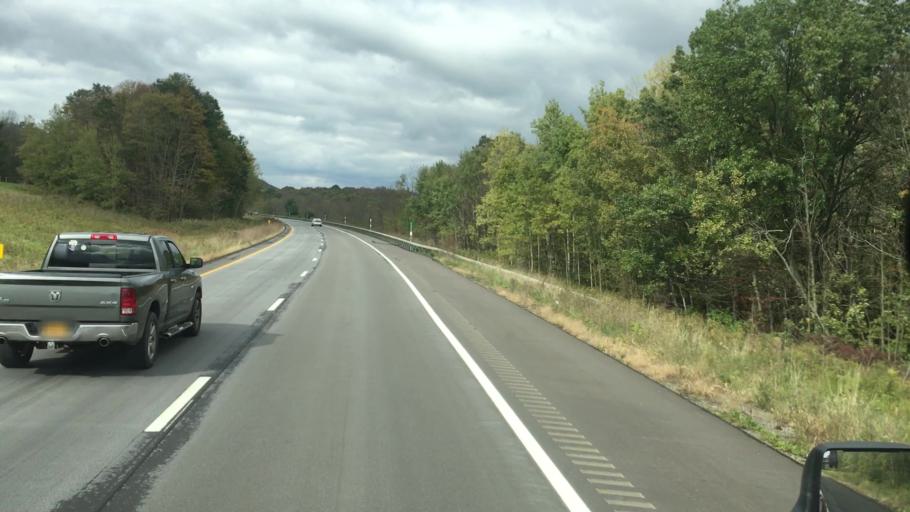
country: US
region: New York
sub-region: Cattaraugus County
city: Randolph
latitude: 42.1158
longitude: -78.9256
